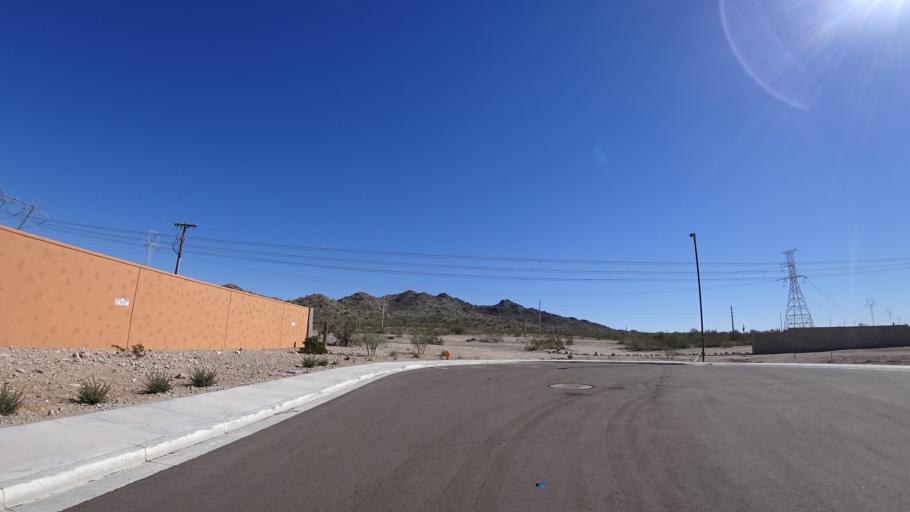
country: US
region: Arizona
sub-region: Maricopa County
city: Goodyear
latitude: 33.3495
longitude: -112.4231
